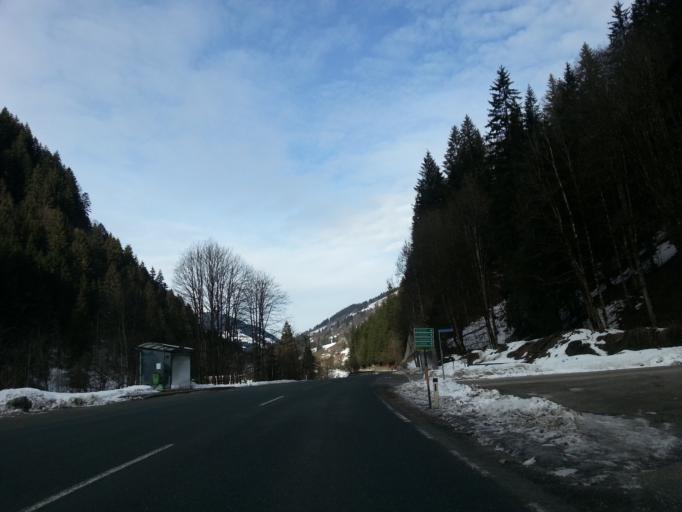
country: AT
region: Salzburg
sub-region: Politischer Bezirk Zell am See
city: Viehhofen
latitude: 47.3644
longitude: 12.7503
